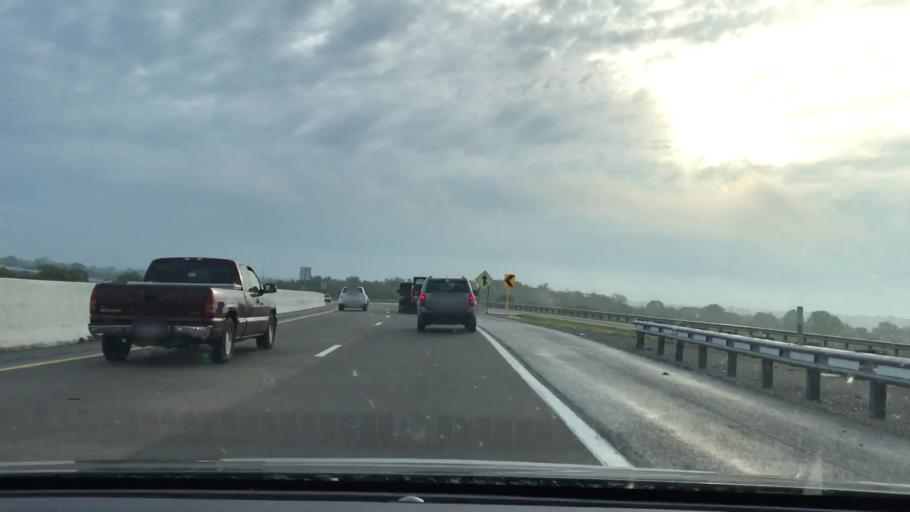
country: US
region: Tennessee
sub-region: Sumner County
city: Hendersonville
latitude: 36.3286
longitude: -86.5563
